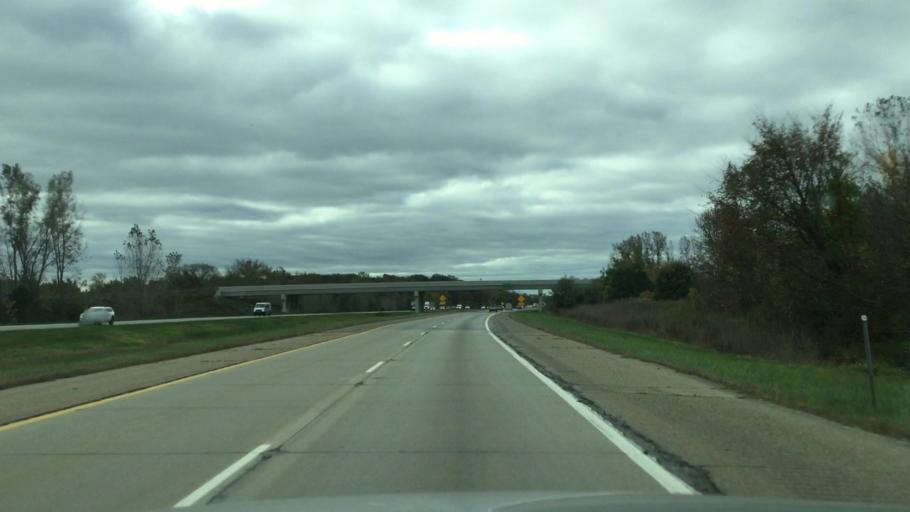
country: US
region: Michigan
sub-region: Macomb County
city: Romeo
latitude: 42.7455
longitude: -83.0212
